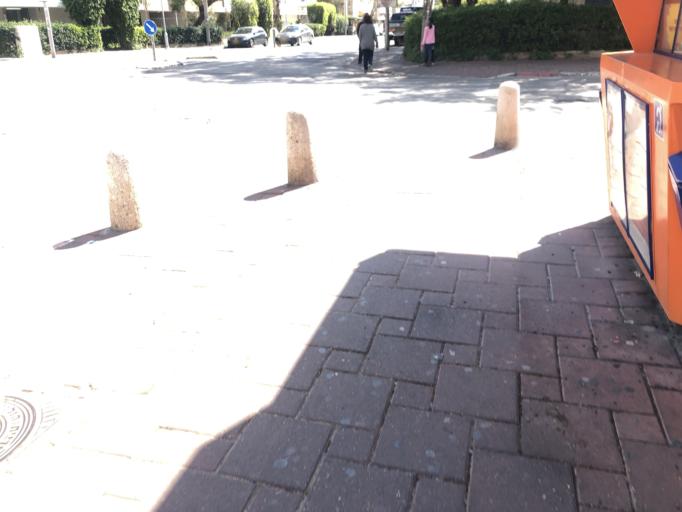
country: IL
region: Tel Aviv
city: Bat Yam
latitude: 32.0210
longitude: 34.7650
